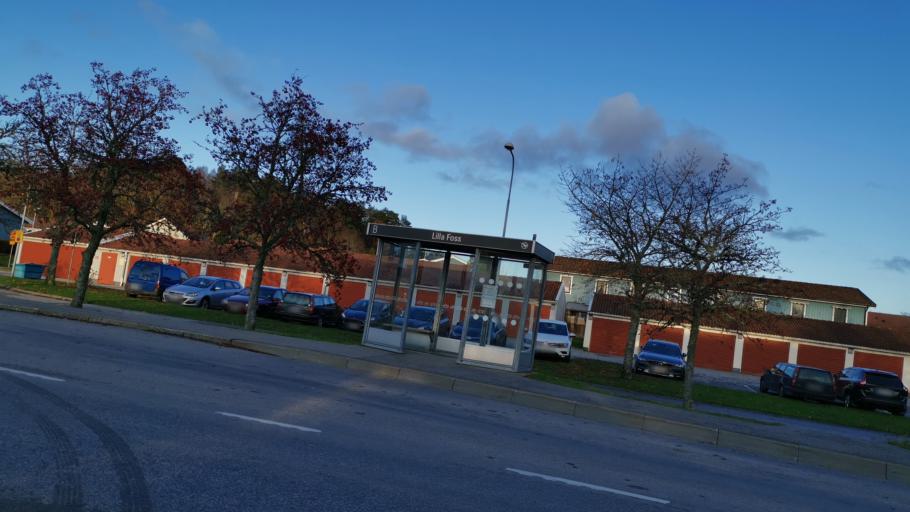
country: SE
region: Vaestra Goetaland
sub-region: Munkedals Kommun
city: Munkedal
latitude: 58.4736
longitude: 11.6672
